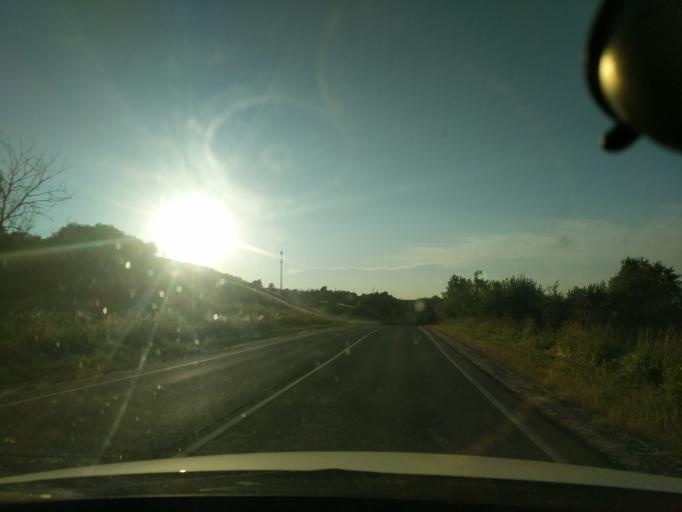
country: RU
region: Moskovskaya
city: Serpukhov
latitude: 54.8537
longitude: 37.4860
